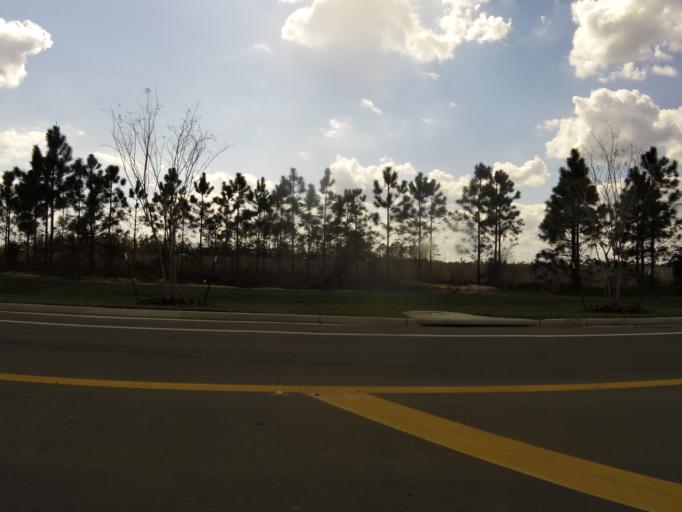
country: US
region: Florida
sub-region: Saint Johns County
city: Palm Valley
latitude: 30.1903
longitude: -81.5044
